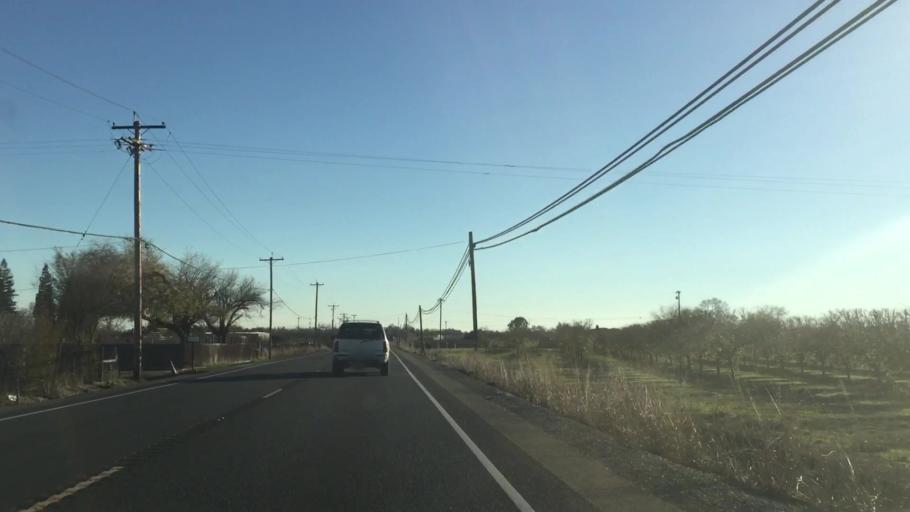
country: US
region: California
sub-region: Yuba County
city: Marysville
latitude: 39.1767
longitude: -121.5912
